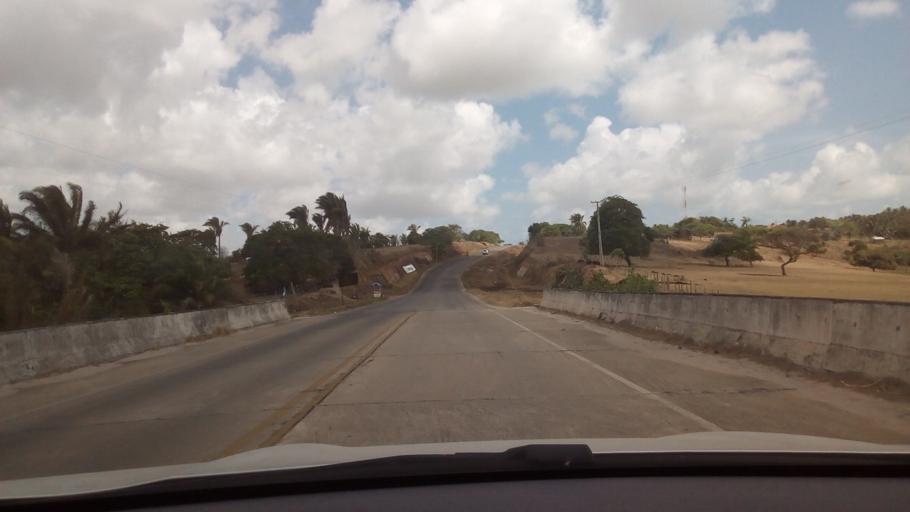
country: BR
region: Paraiba
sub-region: Conde
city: Conde
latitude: -7.2285
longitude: -34.8414
